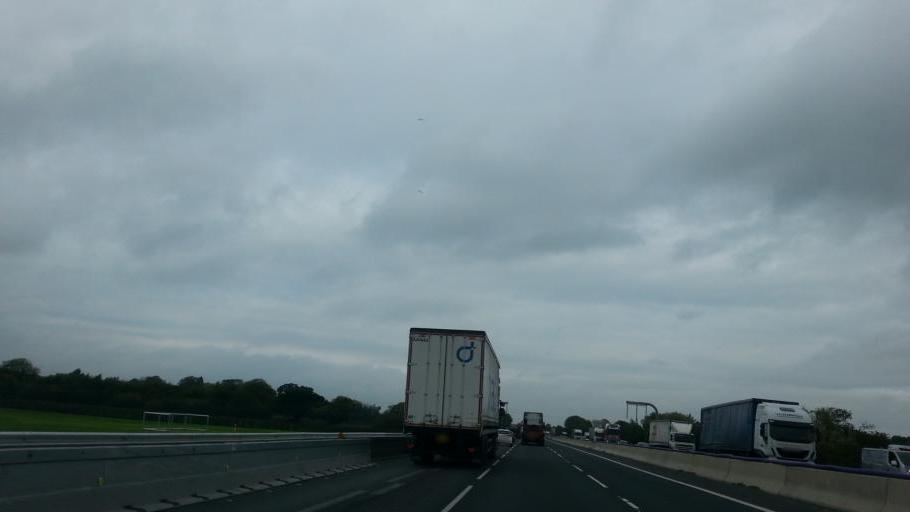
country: GB
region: England
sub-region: Cheshire East
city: Sandbach
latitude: 53.1640
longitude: -2.3547
